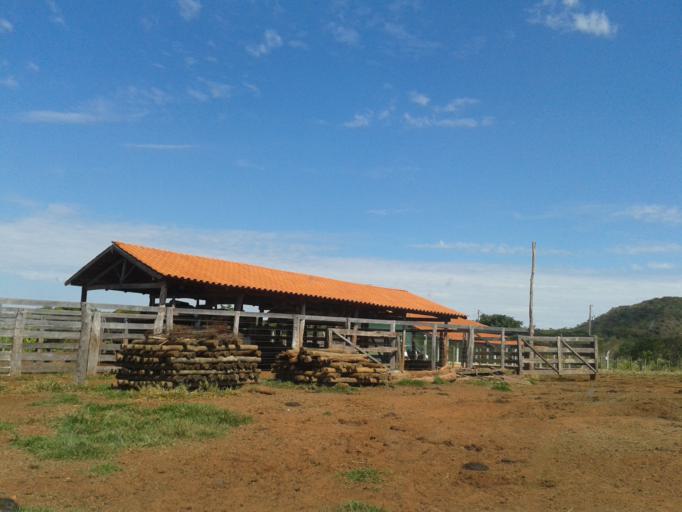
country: BR
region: Minas Gerais
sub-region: Campina Verde
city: Campina Verde
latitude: -19.4035
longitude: -49.7474
